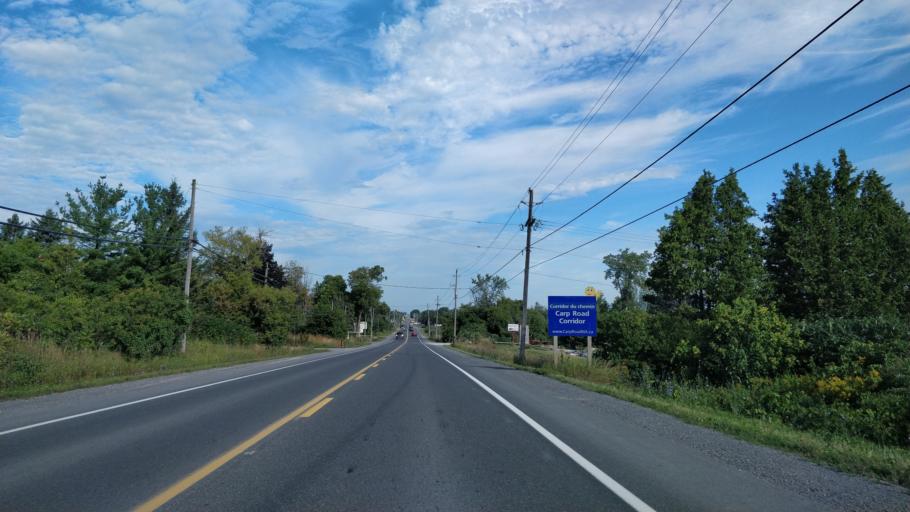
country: CA
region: Ontario
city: Bells Corners
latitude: 45.2877
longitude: -75.9654
